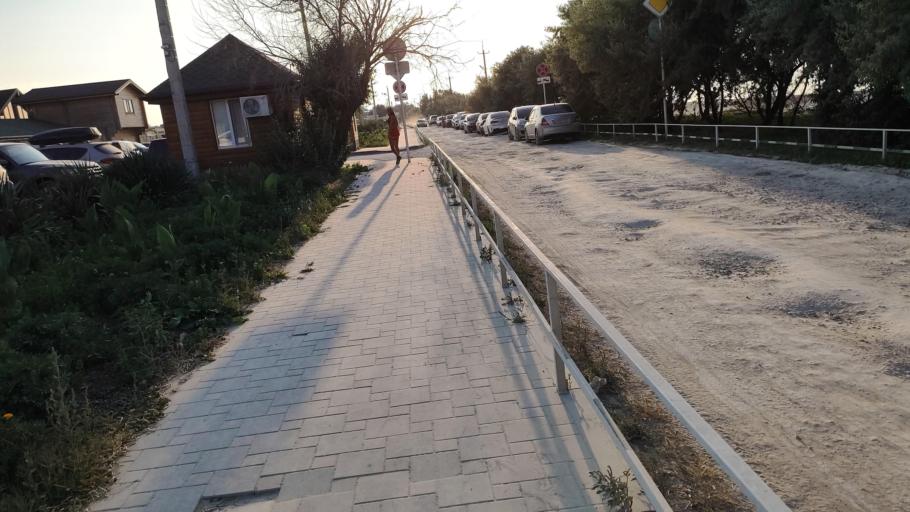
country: RU
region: Krasnodarskiy
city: Blagovetschenskaya
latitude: 45.0655
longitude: 37.0448
